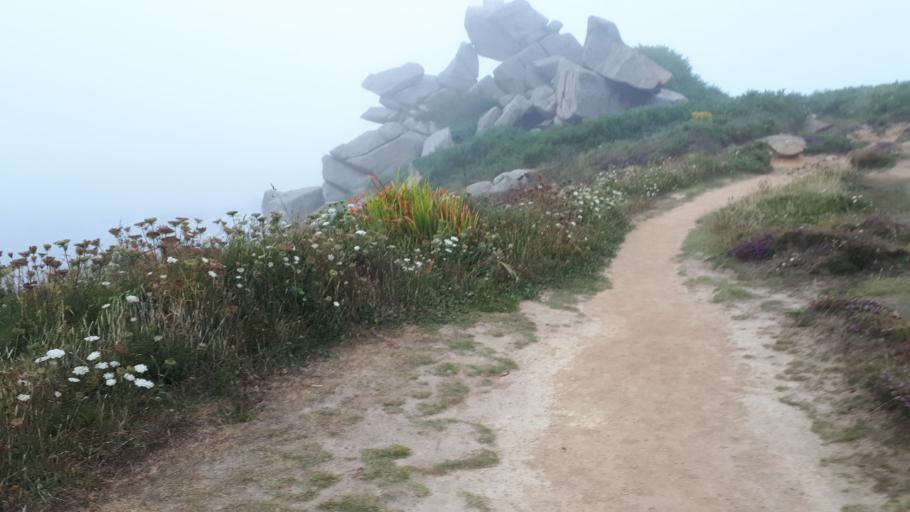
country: FR
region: Brittany
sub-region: Departement du Finistere
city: Plougasnou
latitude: 48.7108
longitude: -3.8332
